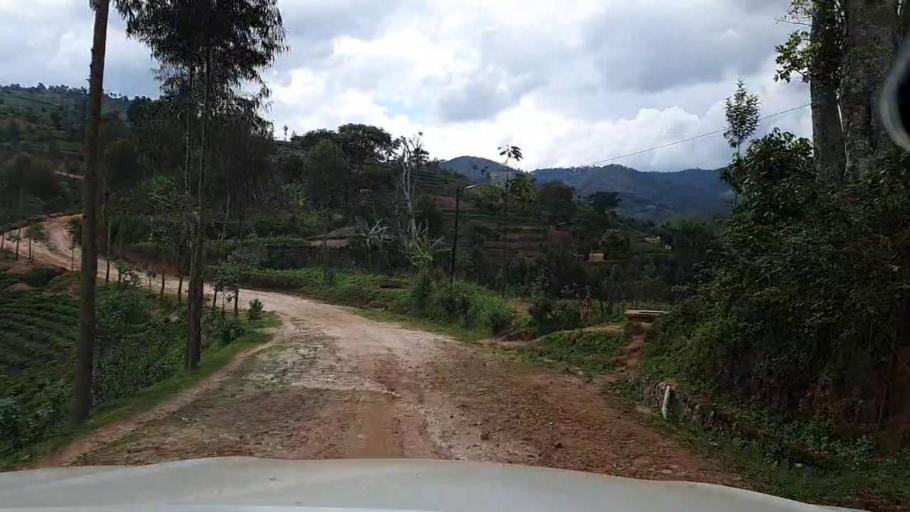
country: RW
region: Southern Province
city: Nzega
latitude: -2.7014
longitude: 29.4358
